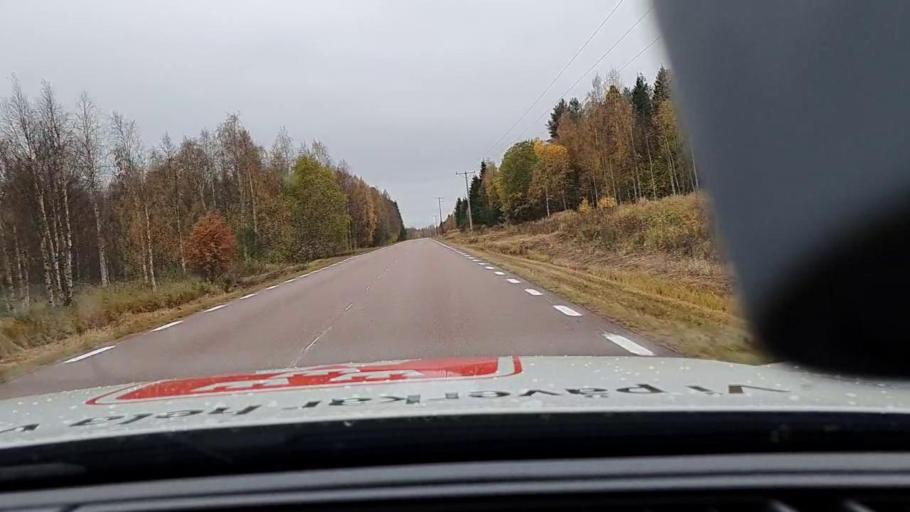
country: FI
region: Lapland
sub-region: Torniolaakso
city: Ylitornio
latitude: 66.1259
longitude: 23.9119
